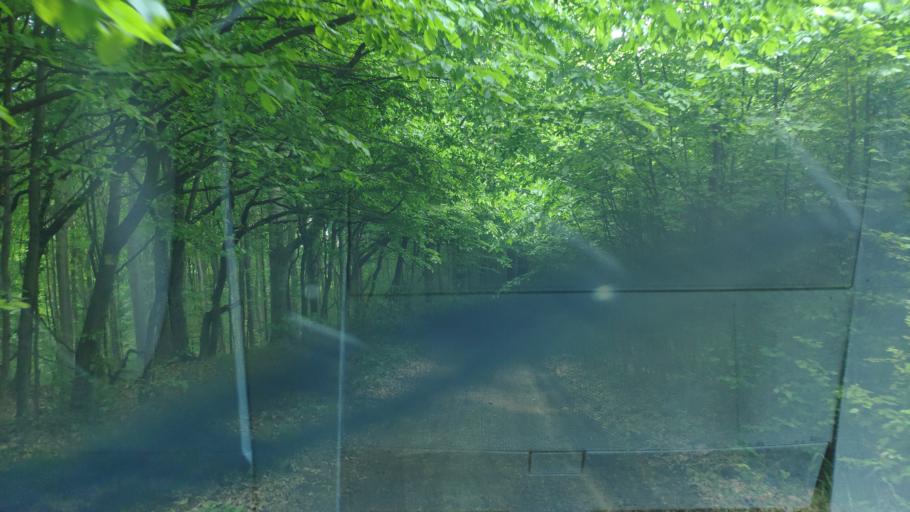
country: SK
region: Presovsky
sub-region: Okres Presov
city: Presov
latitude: 48.9405
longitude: 21.1183
